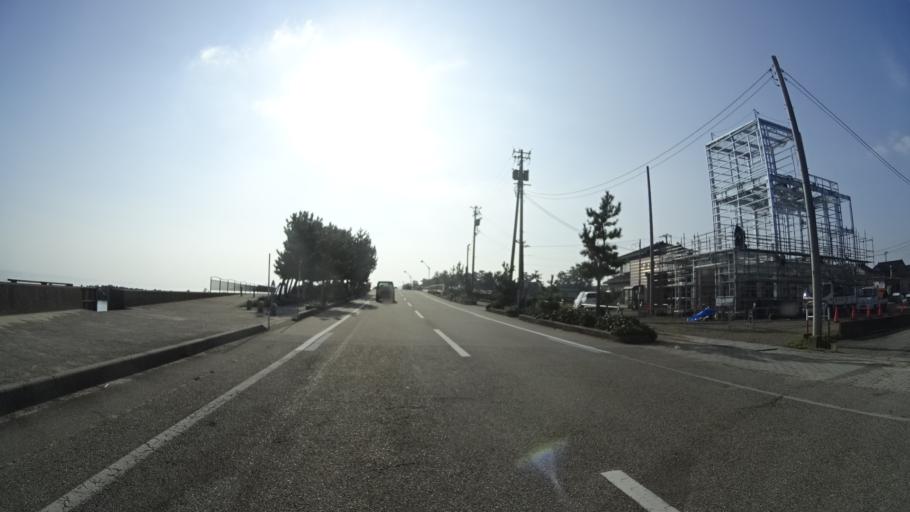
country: JP
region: Toyama
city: Himi
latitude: 36.8490
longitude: 136.9942
